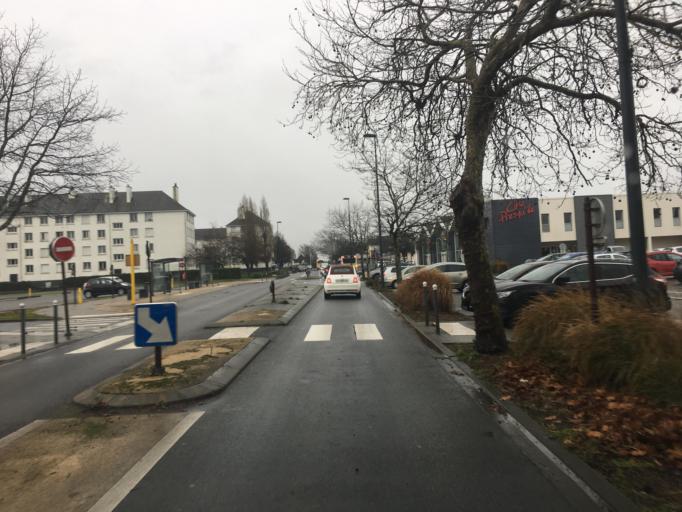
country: FR
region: Pays de la Loire
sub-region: Departement de la Loire-Atlantique
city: Guerande
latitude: 47.3314
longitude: -2.4268
